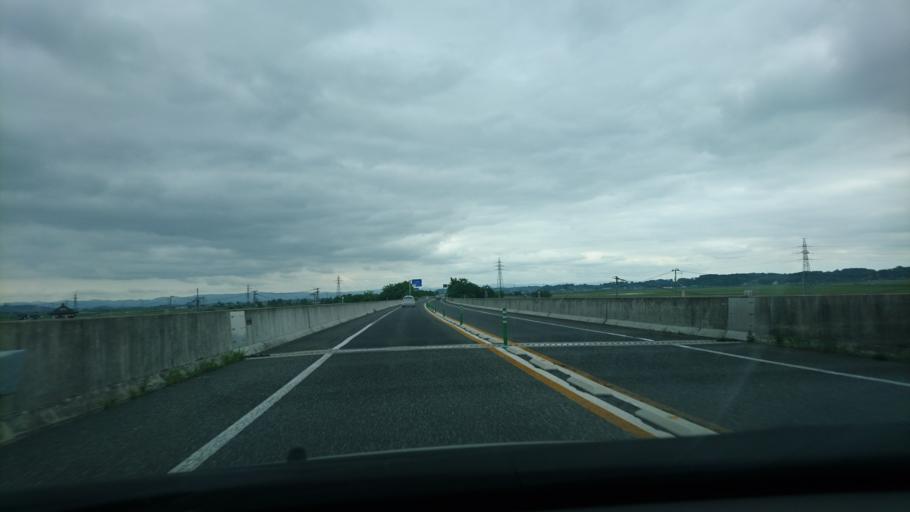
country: JP
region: Iwate
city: Ichinoseki
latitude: 38.7370
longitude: 141.1232
